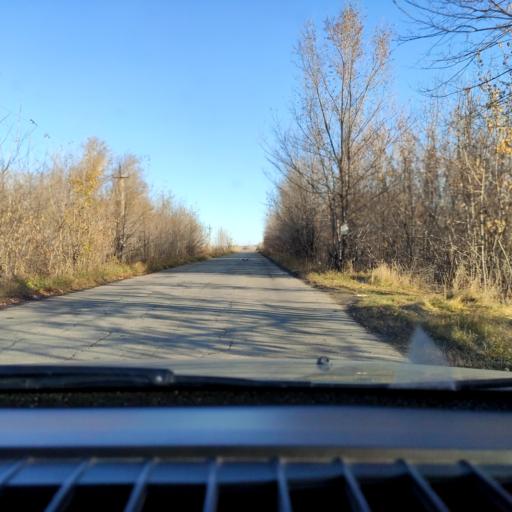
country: RU
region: Samara
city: Tol'yatti
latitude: 53.6405
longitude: 49.3145
